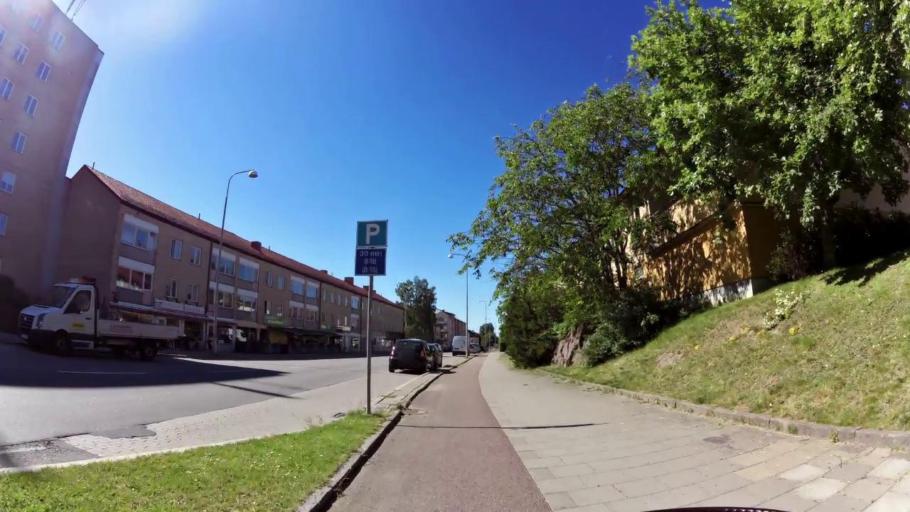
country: SE
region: OEstergoetland
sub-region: Linkopings Kommun
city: Linkoping
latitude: 58.4049
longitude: 15.6442
